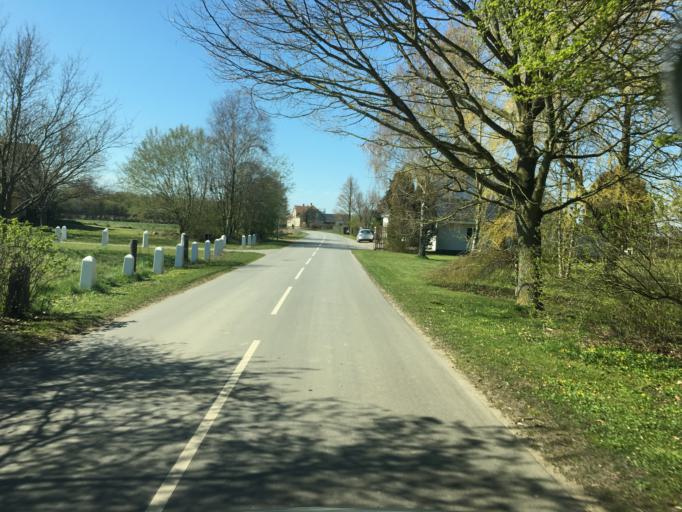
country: DK
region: South Denmark
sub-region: Sonderborg Kommune
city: Dybbol
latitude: 54.9518
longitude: 9.7204
